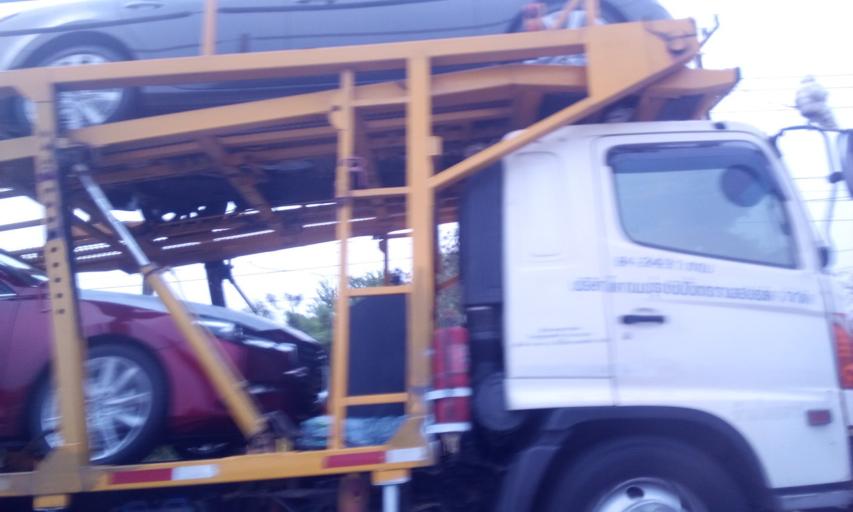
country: TH
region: Chon Buri
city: Ban Bueng
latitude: 13.2428
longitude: 101.2431
